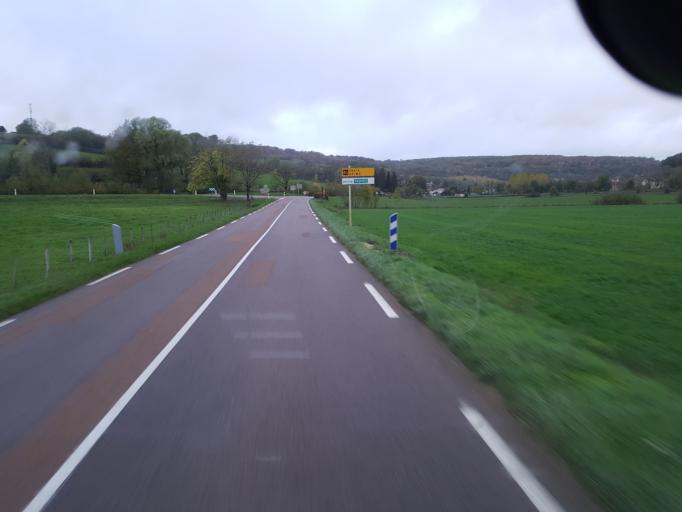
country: FR
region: Bourgogne
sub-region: Departement de la Cote-d'Or
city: Chatillon-sur-Seine
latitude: 47.6964
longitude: 4.6148
